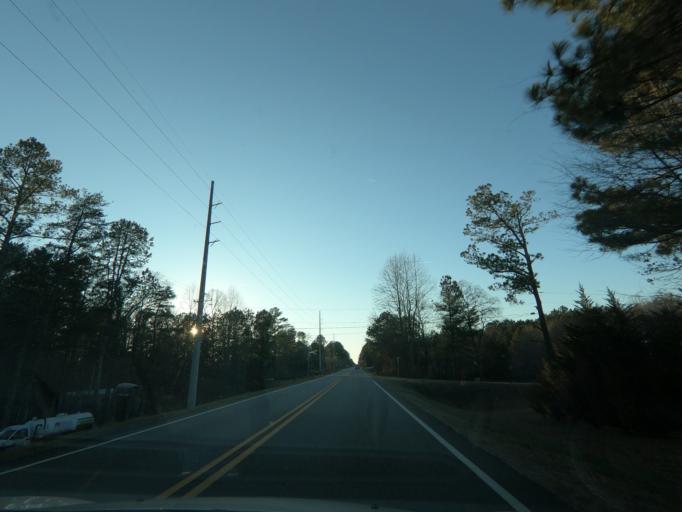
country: US
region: Georgia
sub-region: Dawson County
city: Dawsonville
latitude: 34.3539
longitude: -84.0773
